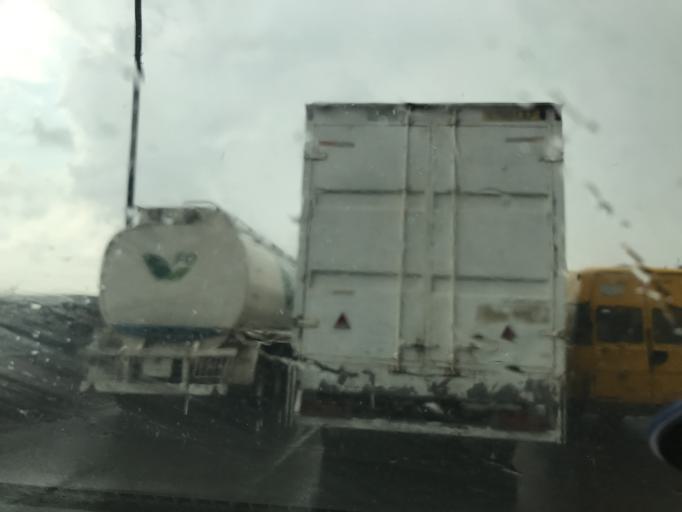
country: NG
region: Lagos
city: Oshodi
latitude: 6.5544
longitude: 3.3486
